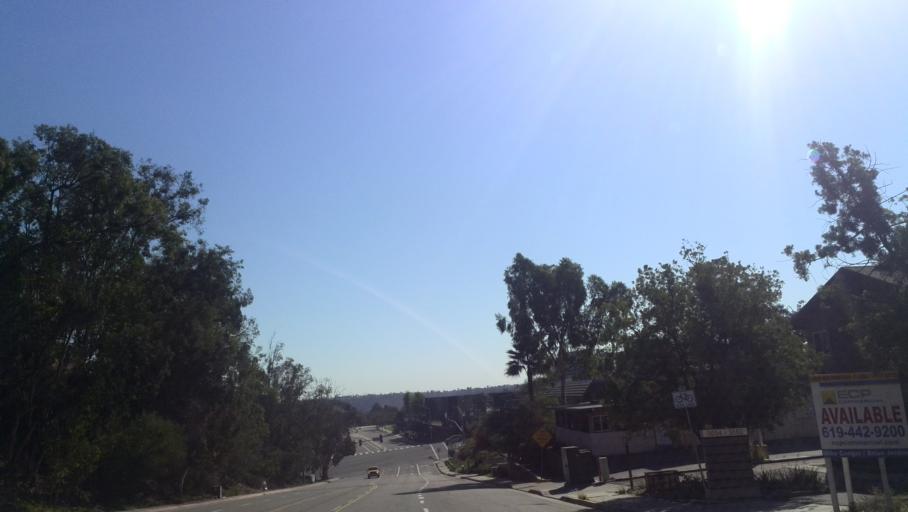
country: US
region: California
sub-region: San Diego County
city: San Diego
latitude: 32.8106
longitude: -117.1196
